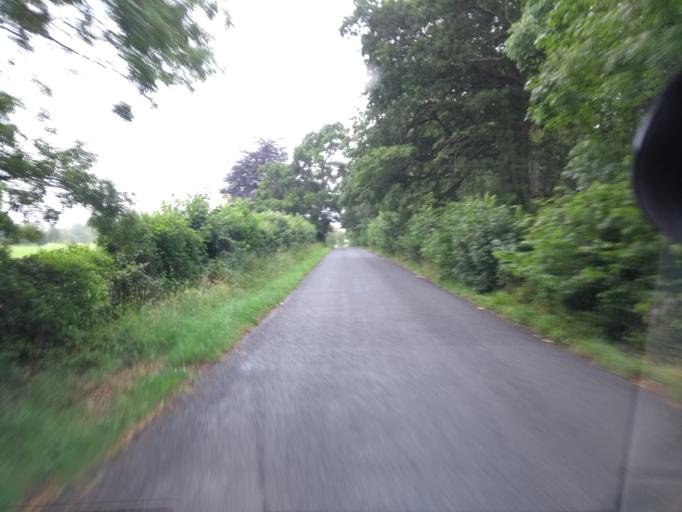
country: GB
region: England
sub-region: Somerset
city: Street
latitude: 51.0801
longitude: -2.6840
